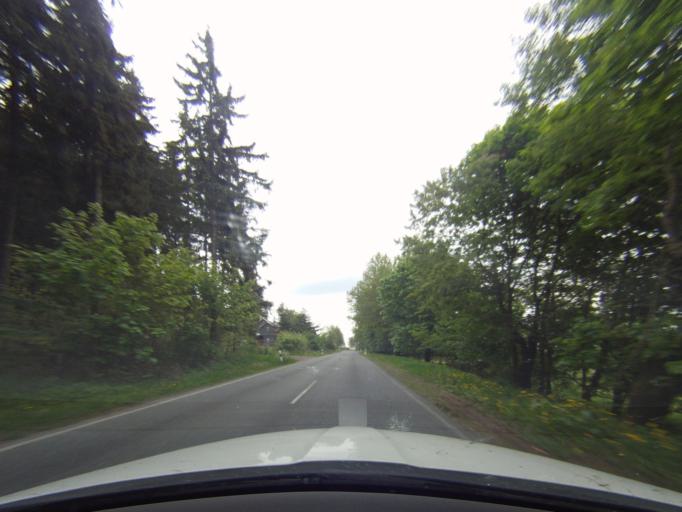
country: DE
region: Thuringia
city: Gillersdorf
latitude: 50.6172
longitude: 11.0275
